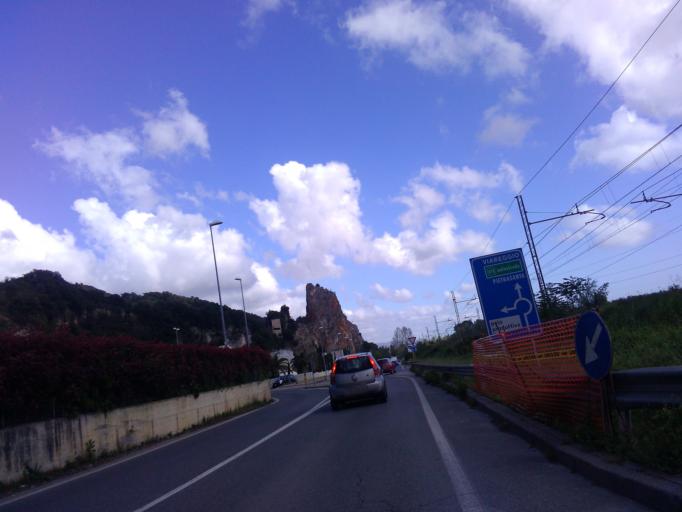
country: IT
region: Tuscany
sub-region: Provincia di Massa-Carrara
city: Capanne-Prato-Cinquale
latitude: 44.0005
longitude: 10.1684
